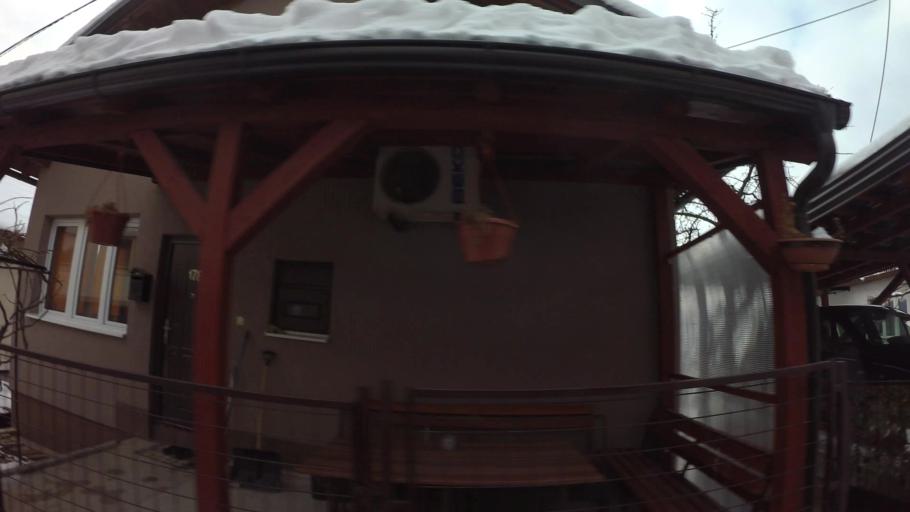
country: BA
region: Federation of Bosnia and Herzegovina
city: Kobilja Glava
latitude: 43.8623
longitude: 18.3779
